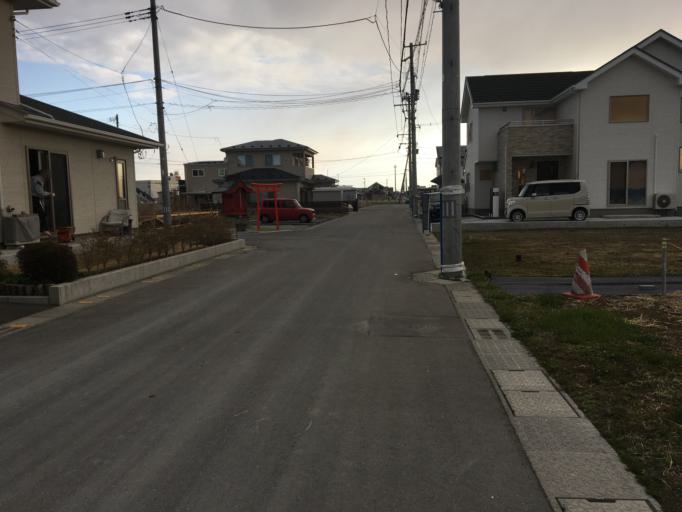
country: JP
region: Aomori
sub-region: Hachinohe Shi
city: Uchimaru
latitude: 40.5090
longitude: 141.4286
